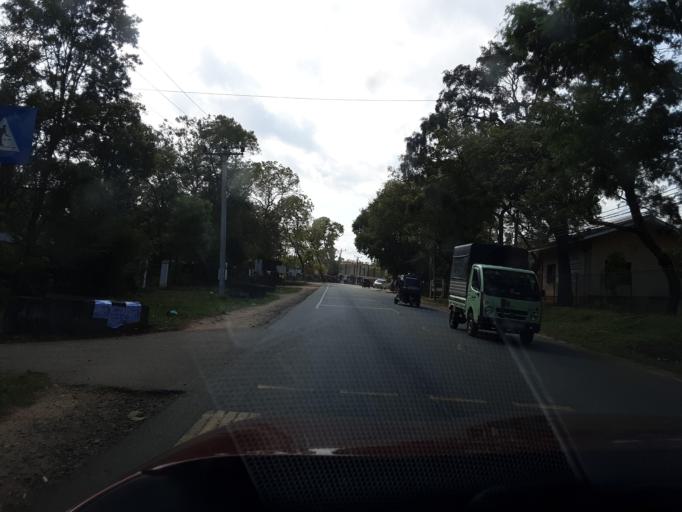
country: LK
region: Uva
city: Haputale
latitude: 6.3464
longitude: 81.1977
